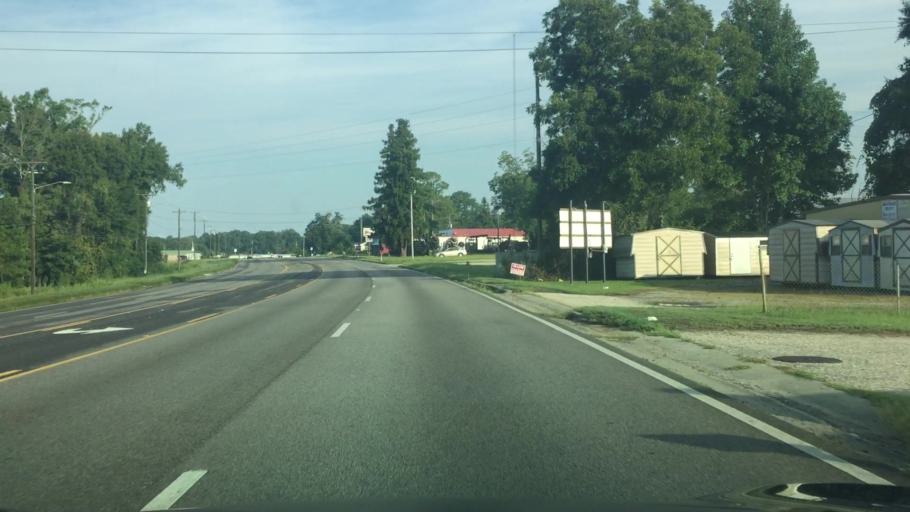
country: US
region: Alabama
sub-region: Covington County
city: Andalusia
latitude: 31.3203
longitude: -86.5005
